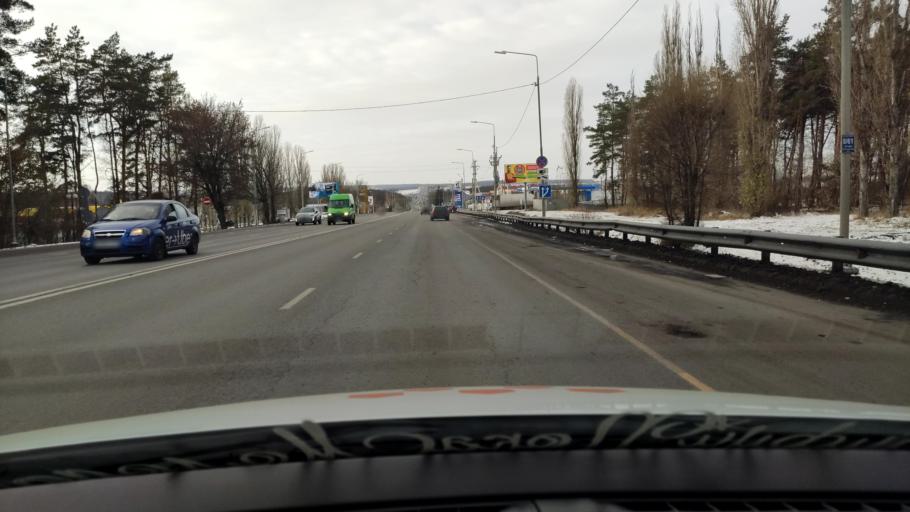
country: RU
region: Voronezj
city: Pridonskoy
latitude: 51.6483
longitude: 39.0981
